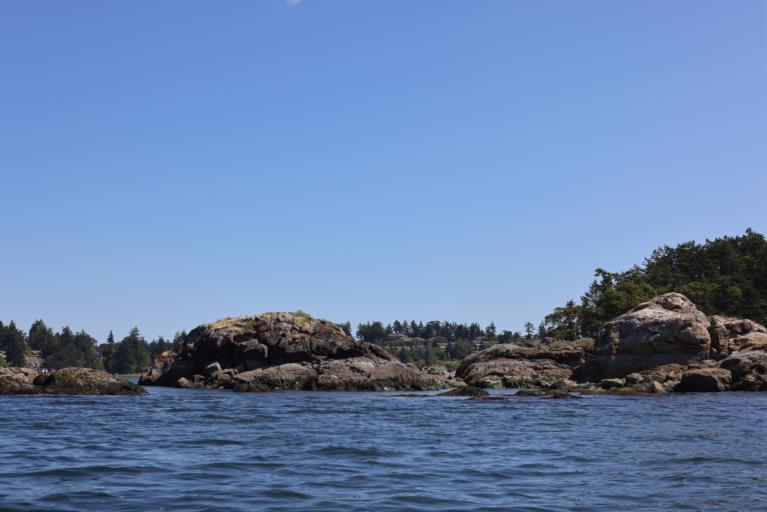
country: CA
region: British Columbia
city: Colwood
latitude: 48.4416
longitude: -123.4410
